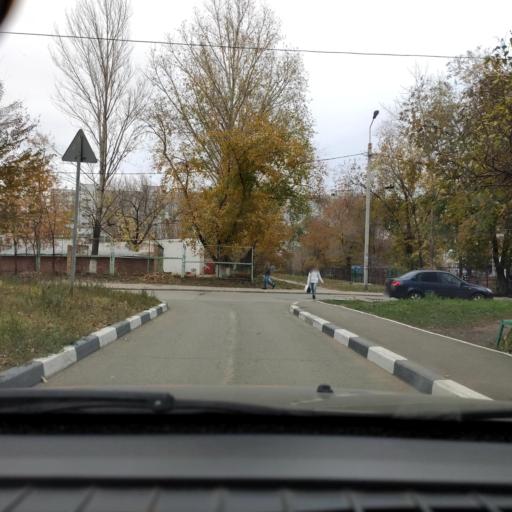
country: RU
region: Samara
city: Zhigulevsk
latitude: 53.4783
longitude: 49.4807
